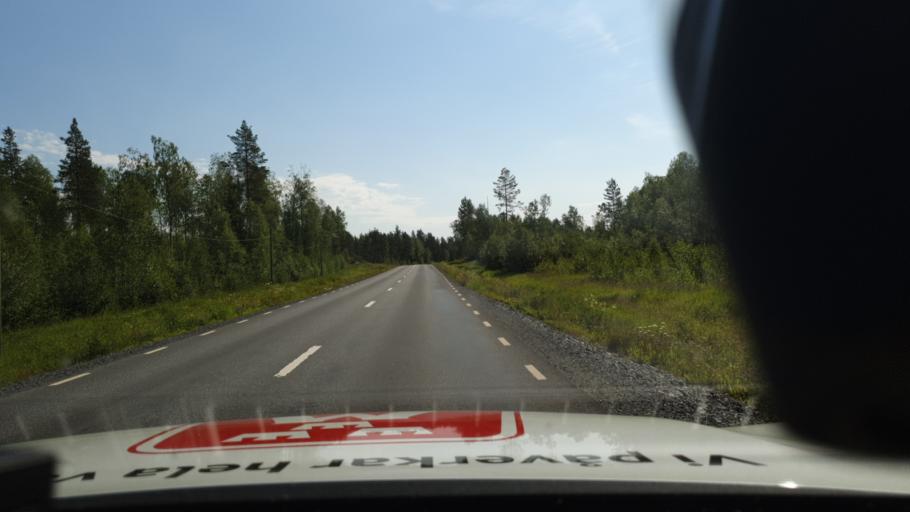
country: SE
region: Norrbotten
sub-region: Lulea Kommun
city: Ranea
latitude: 65.7902
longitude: 22.1382
